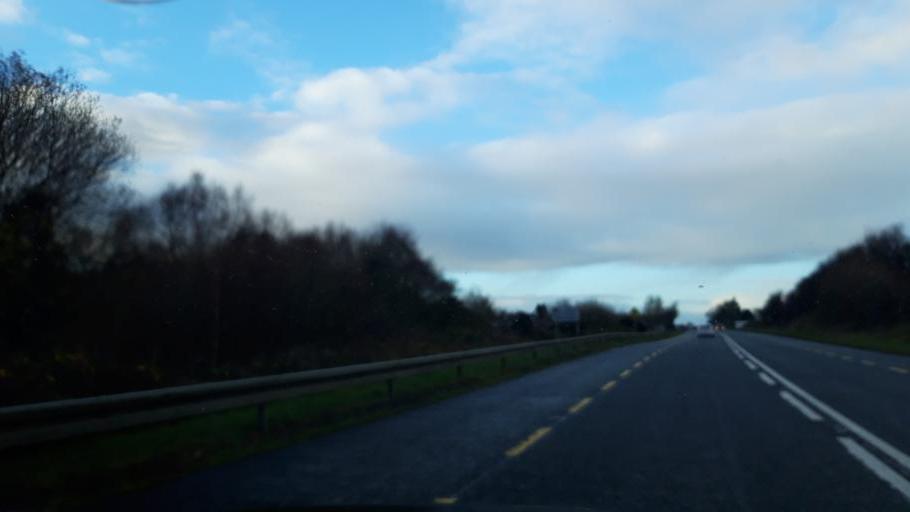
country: IE
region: Ulster
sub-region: County Monaghan
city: Carrickmacross
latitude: 53.9325
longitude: -6.6515
